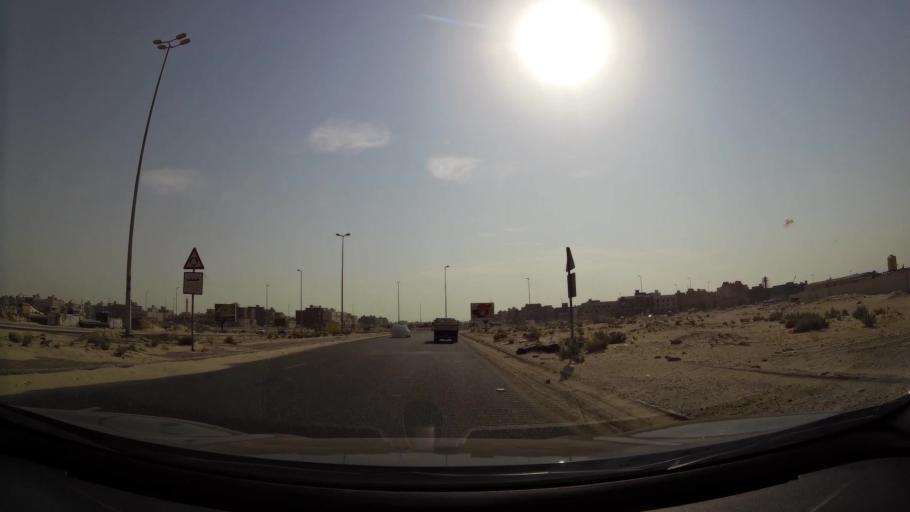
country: KW
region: Al Ahmadi
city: Al Wafrah
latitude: 28.7920
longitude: 48.0357
